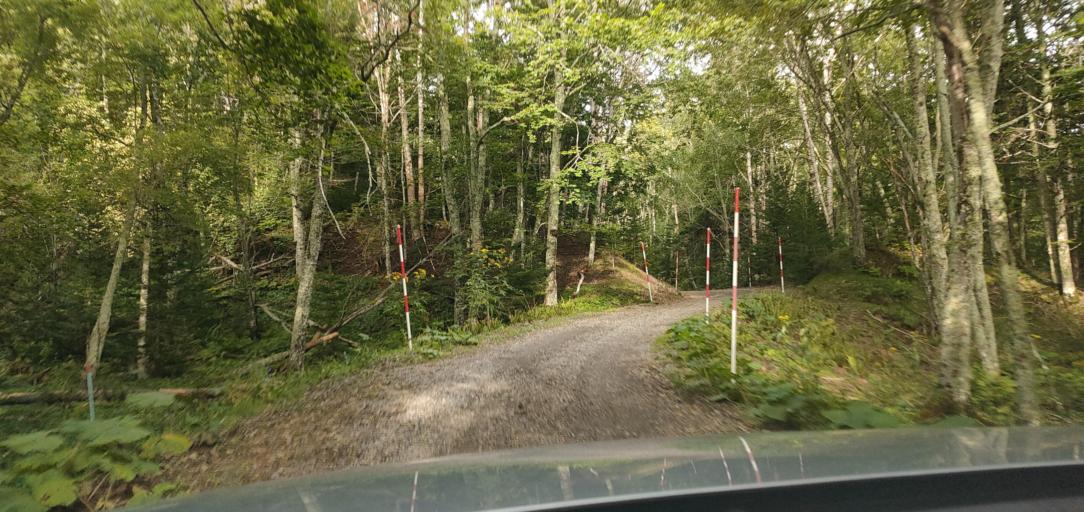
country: JP
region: Hokkaido
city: Kitami
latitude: 43.3730
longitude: 143.9592
